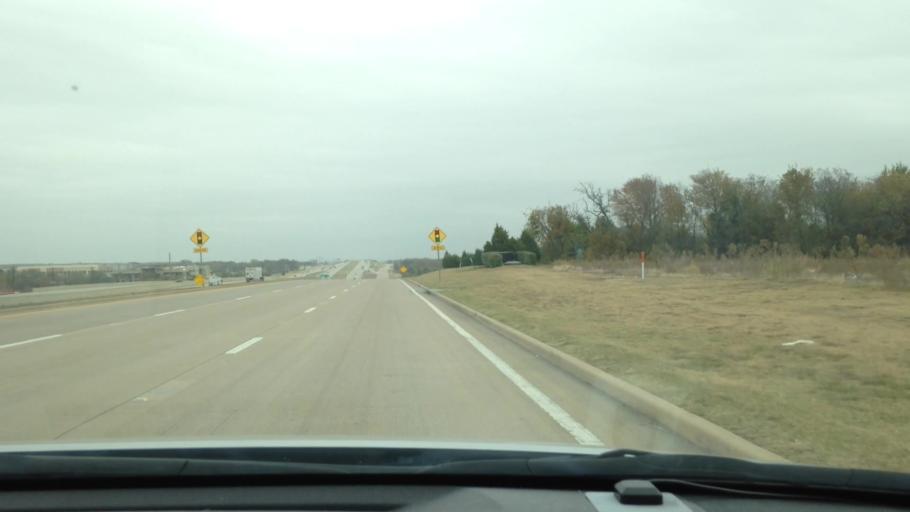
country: US
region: Texas
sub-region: Collin County
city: Allen
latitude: 33.1271
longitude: -96.7257
